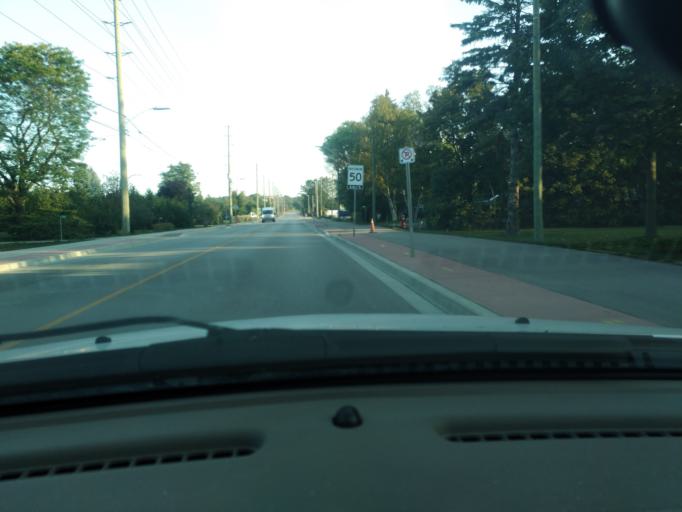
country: CA
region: Ontario
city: Bradford West Gwillimbury
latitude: 44.0952
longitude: -79.5676
